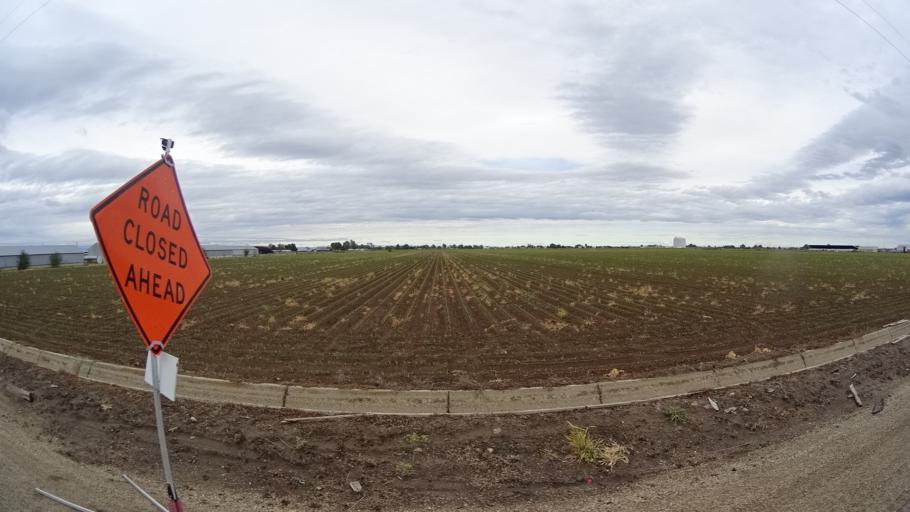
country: US
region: Idaho
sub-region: Ada County
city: Star
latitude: 43.6366
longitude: -116.4936
